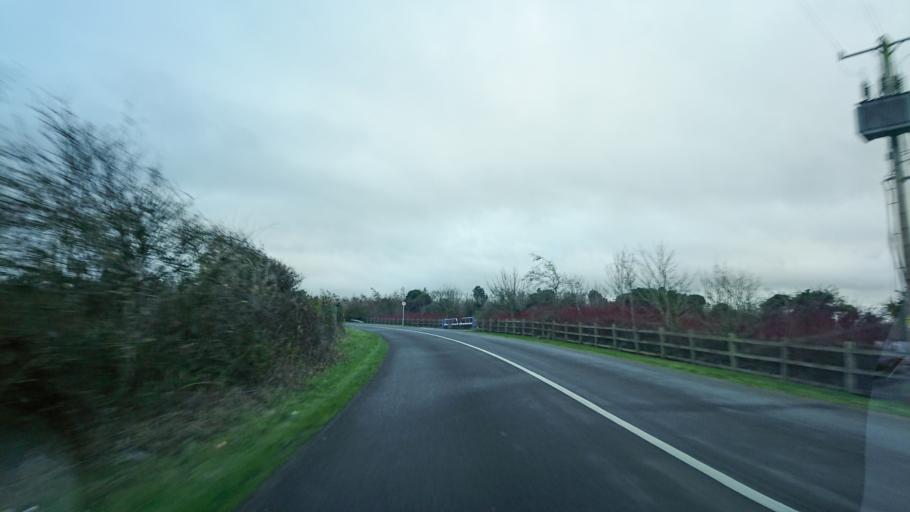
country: IE
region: Munster
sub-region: Waterford
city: Portlaw
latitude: 52.1982
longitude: -7.4276
